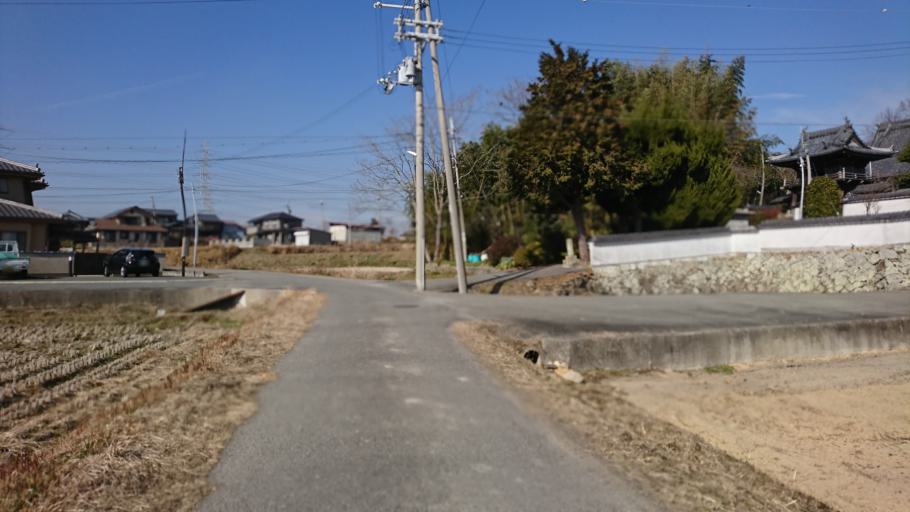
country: JP
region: Hyogo
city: Kakogawacho-honmachi
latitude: 34.8081
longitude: 134.8639
